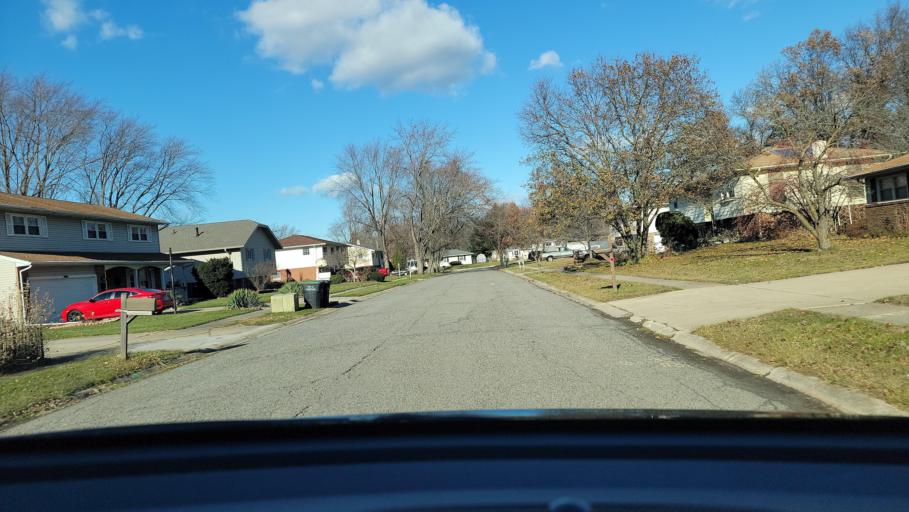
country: US
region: Indiana
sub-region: Porter County
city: Portage
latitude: 41.5637
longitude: -87.1871
